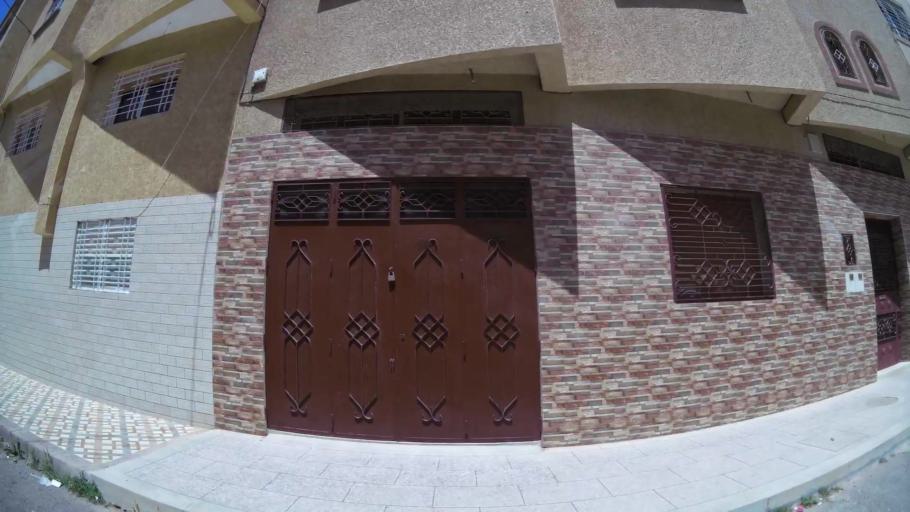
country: MA
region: Oriental
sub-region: Oujda-Angad
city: Oujda
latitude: 34.6941
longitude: -1.8892
